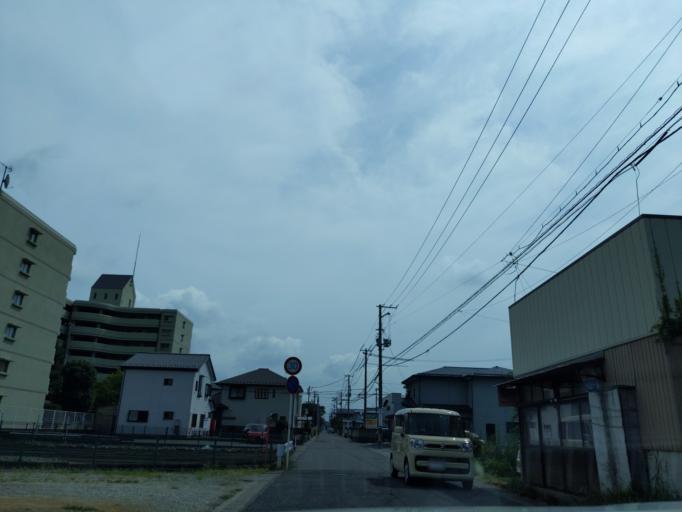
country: JP
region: Fukushima
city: Koriyama
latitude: 37.3959
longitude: 140.3425
